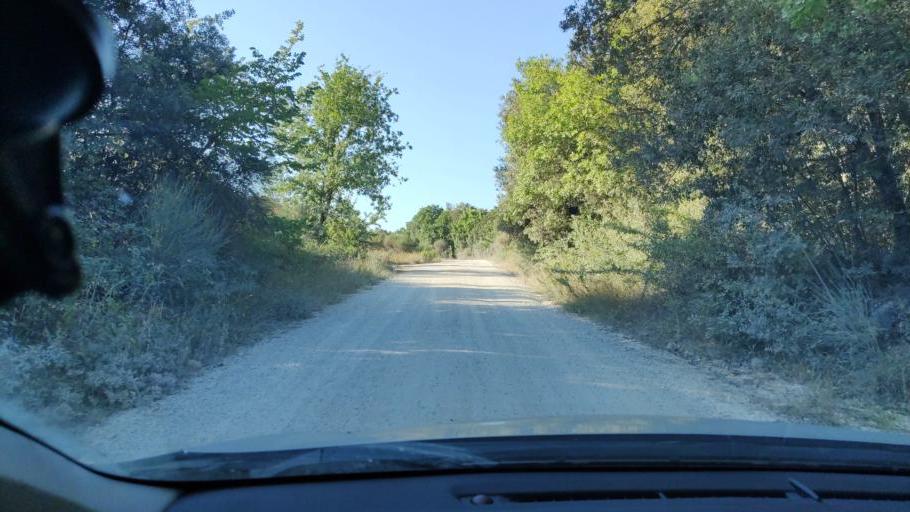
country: IT
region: Umbria
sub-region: Provincia di Terni
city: Amelia
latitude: 42.5373
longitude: 12.3793
